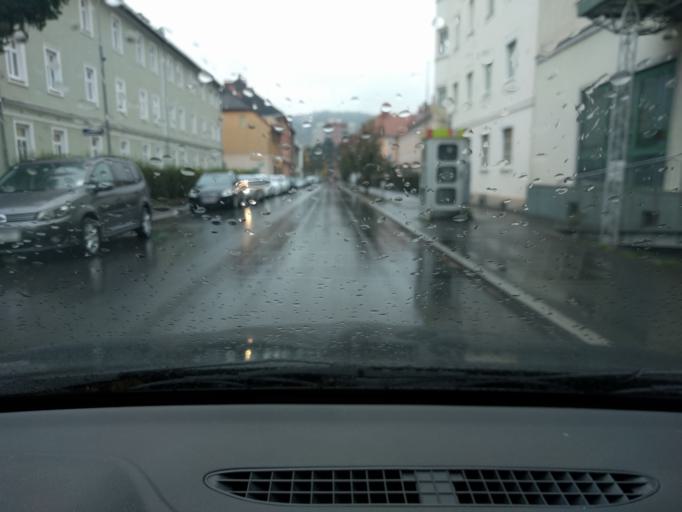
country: AT
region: Styria
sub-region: Politischer Bezirk Leoben
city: Leoben
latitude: 47.3847
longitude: 15.1012
